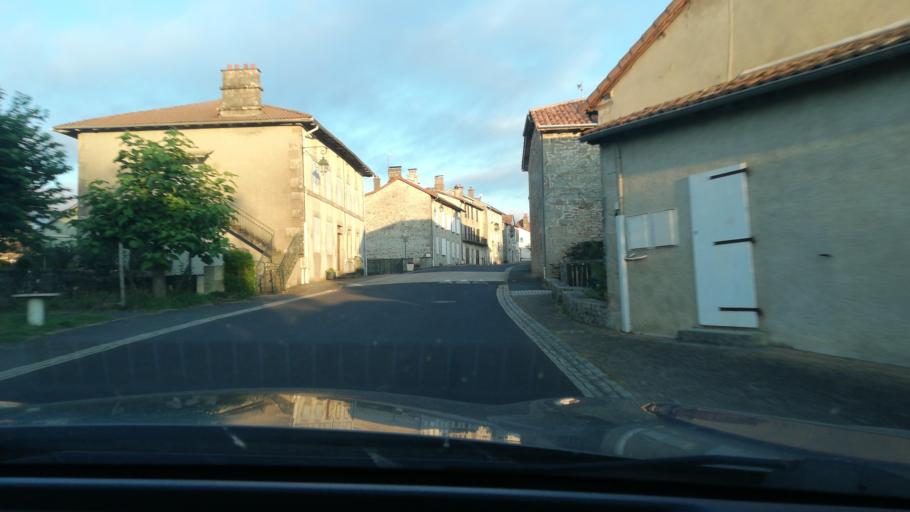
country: FR
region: Auvergne
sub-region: Departement du Cantal
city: Laroquebrou
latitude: 44.9557
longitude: 2.1253
